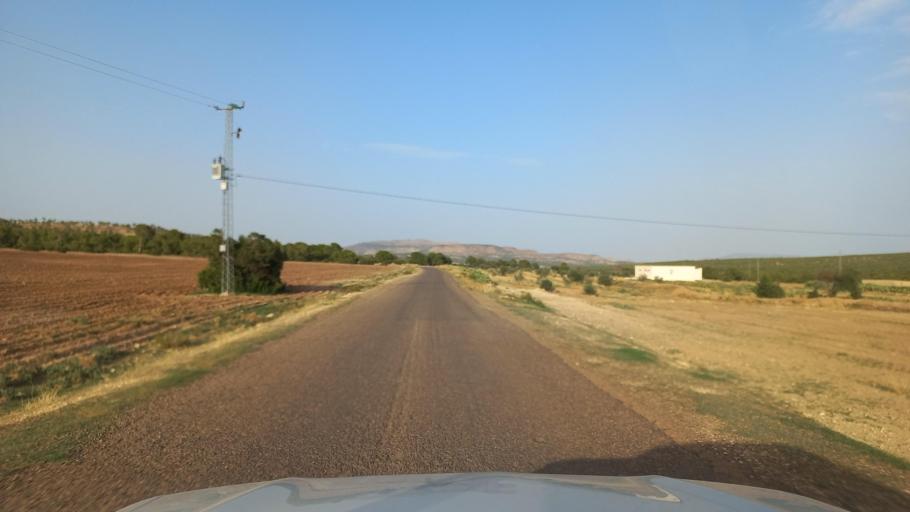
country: TN
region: Al Qasrayn
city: Kasserine
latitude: 35.3970
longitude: 8.8838
